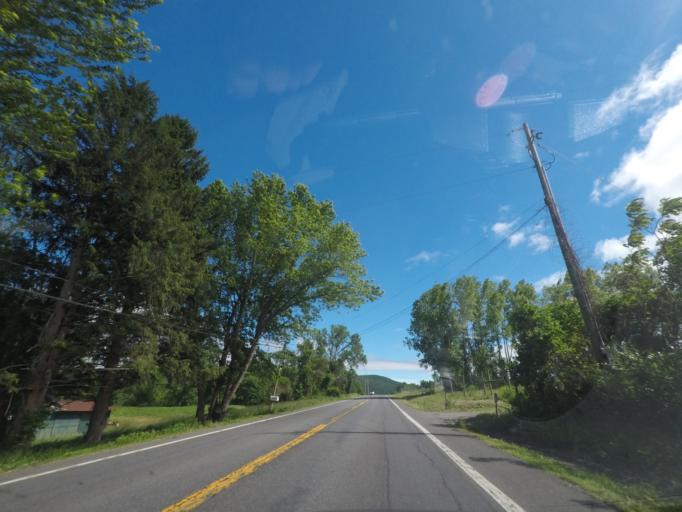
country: US
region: New York
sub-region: Columbia County
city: Philmont
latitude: 42.1317
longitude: -73.5267
